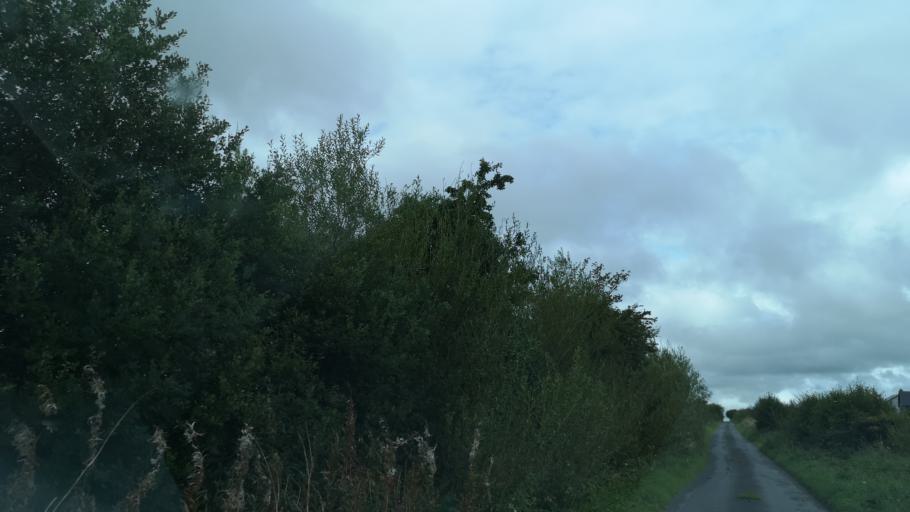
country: IE
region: Connaught
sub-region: County Galway
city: Loughrea
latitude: 53.3043
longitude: -8.5820
